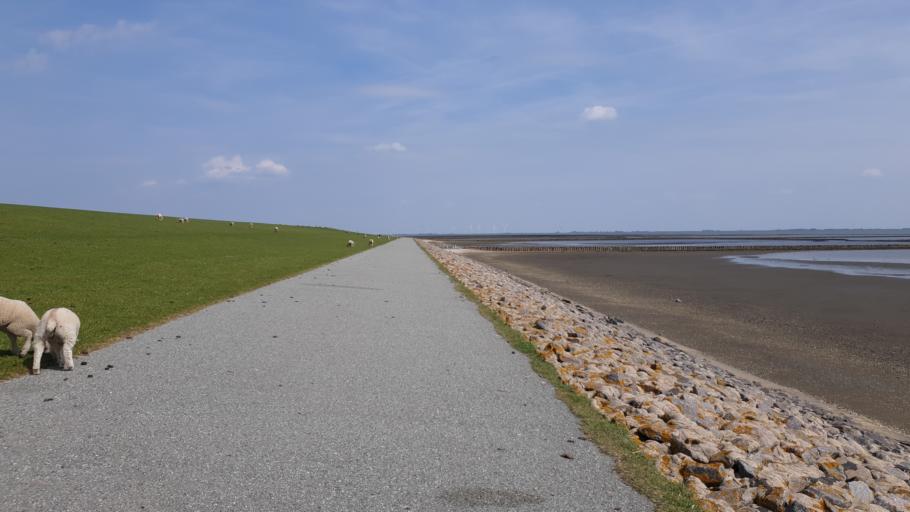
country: DE
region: Schleswig-Holstein
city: Elisabeth-Sophien-Koog
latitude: 54.4606
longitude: 8.8594
